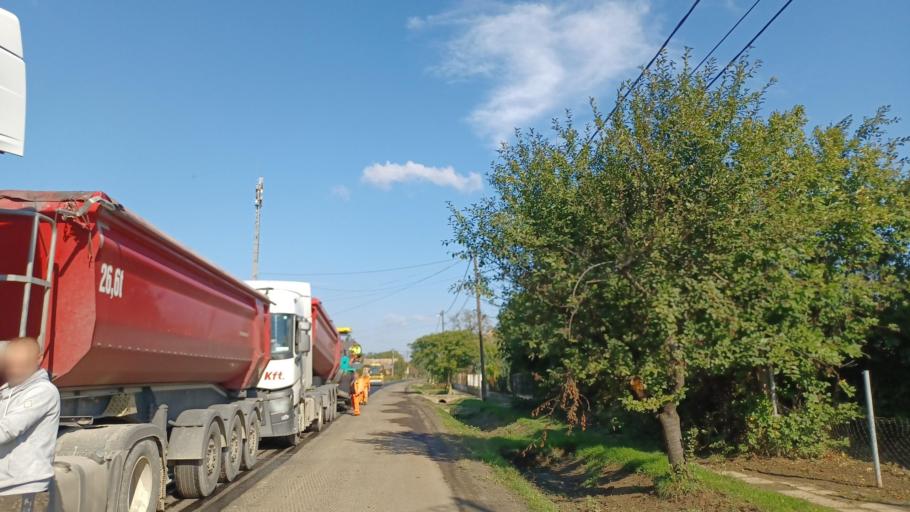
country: HU
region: Tolna
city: Nagydorog
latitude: 46.6030
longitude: 18.5938
